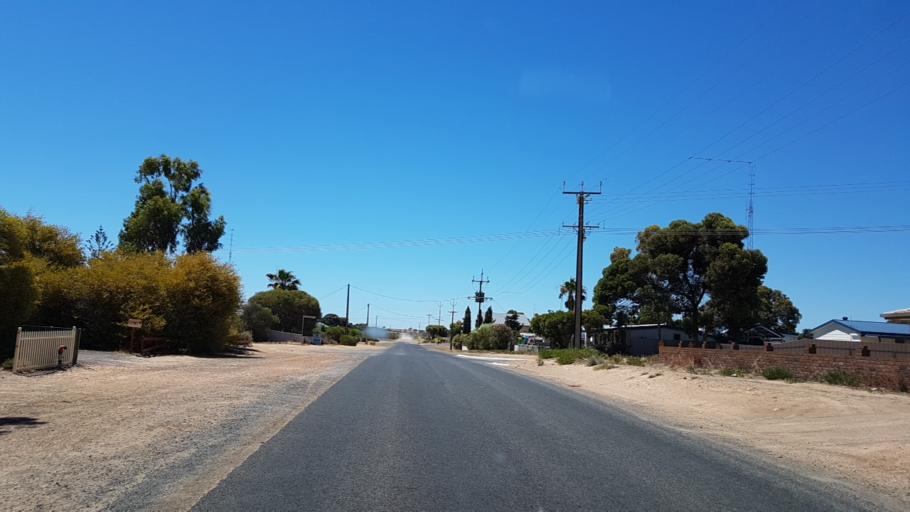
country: AU
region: South Australia
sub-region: Copper Coast
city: Wallaroo
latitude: -34.0498
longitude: 137.5680
